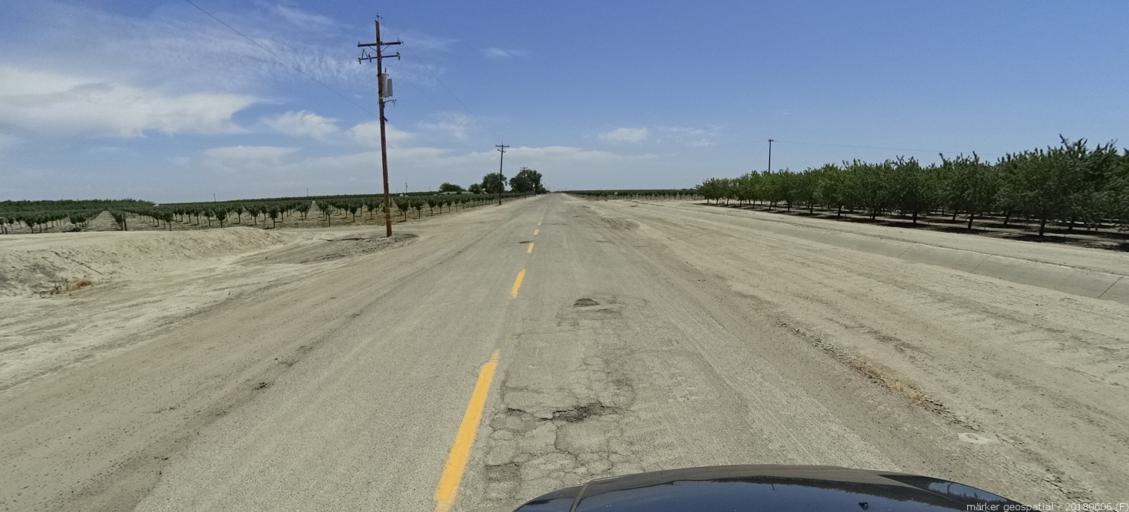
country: US
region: California
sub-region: Fresno County
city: Firebaugh
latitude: 36.8367
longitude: -120.3960
